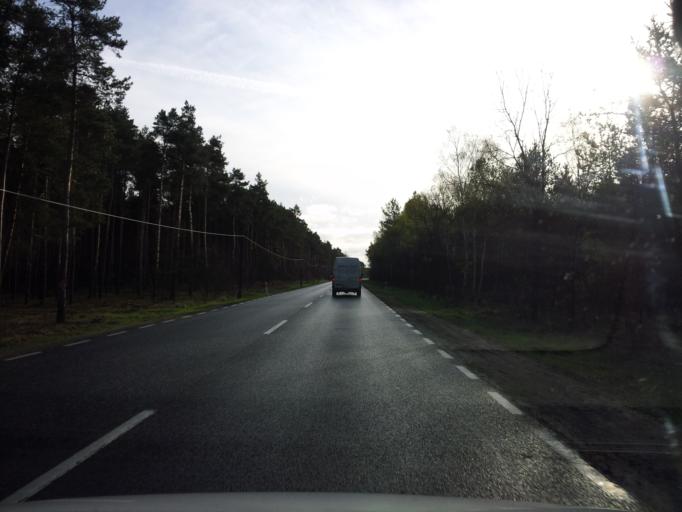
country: PL
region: Lubusz
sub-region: Powiat zielonogorski
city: Nowogrod Bobrzanski
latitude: 51.8132
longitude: 15.2738
